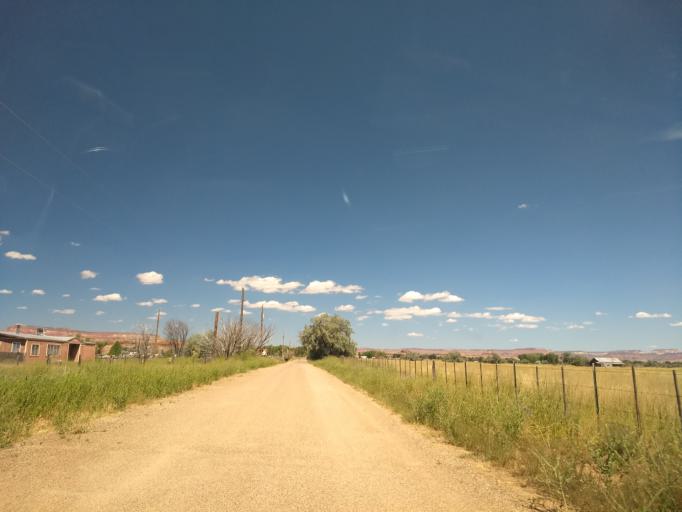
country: US
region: Arizona
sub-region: Coconino County
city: Fredonia
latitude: 36.9308
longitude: -112.5353
